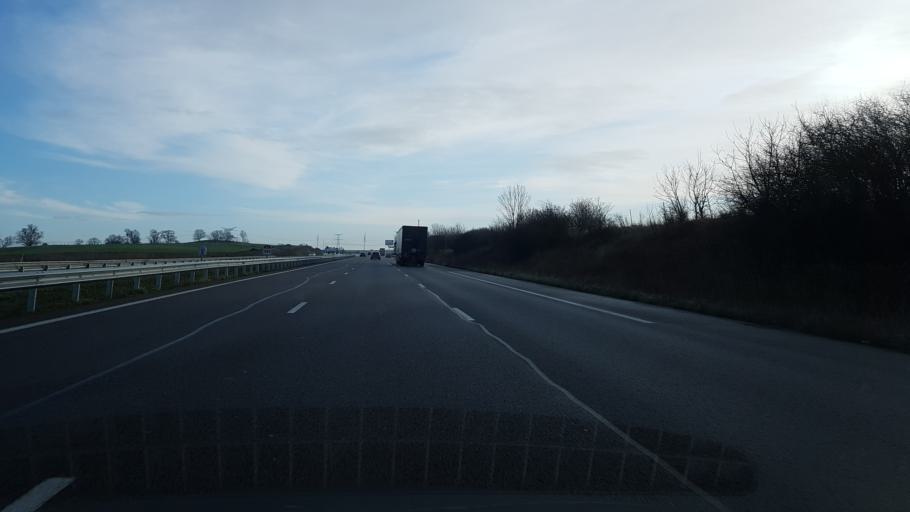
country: FR
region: Lorraine
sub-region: Departement de la Moselle
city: Courcelles-Chaussy
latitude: 49.1400
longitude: 6.4556
